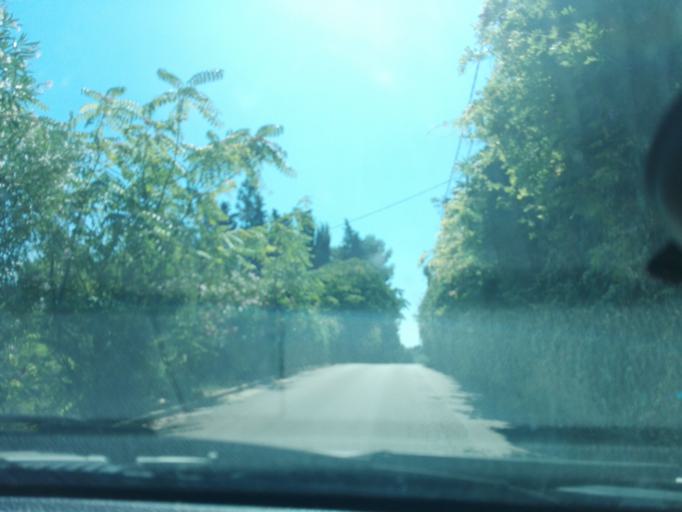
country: IT
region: Abruzzo
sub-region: Provincia di Pescara
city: Montesilvano Marina
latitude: 42.4964
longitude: 14.1592
